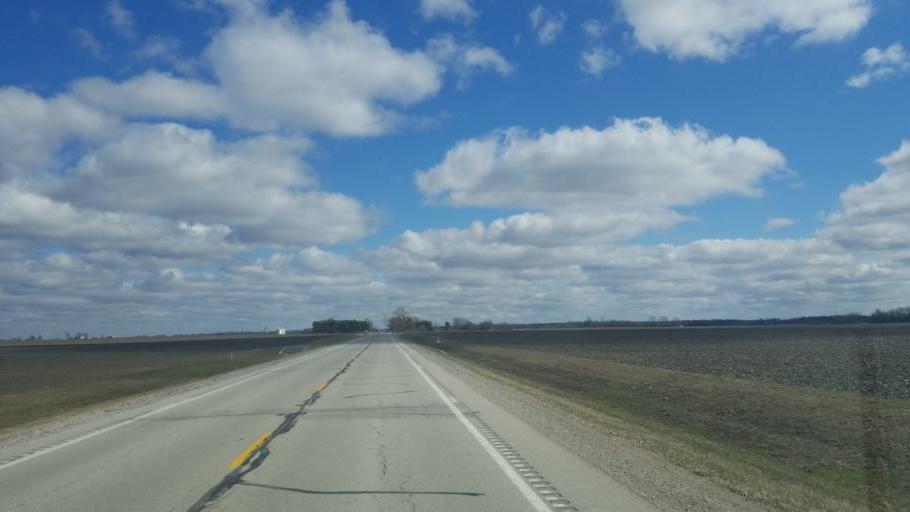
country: US
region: Illinois
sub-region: Douglas County
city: Villa Grove
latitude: 39.7921
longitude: -88.0449
